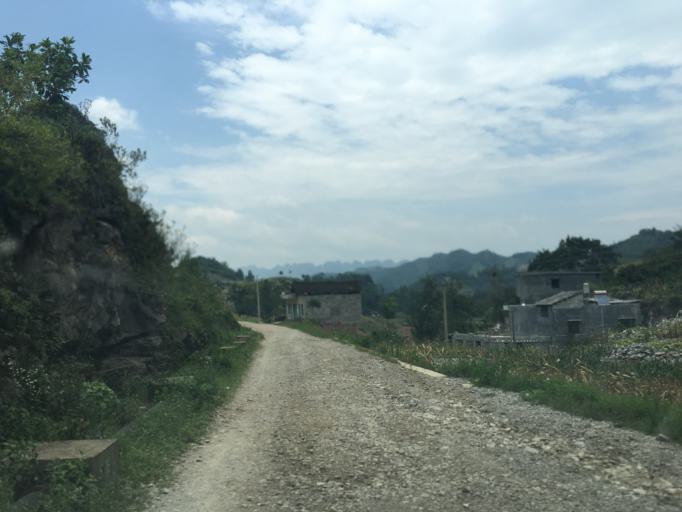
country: CN
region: Guangxi Zhuangzu Zizhiqu
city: Xinzhou
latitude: 25.2861
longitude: 105.6369
